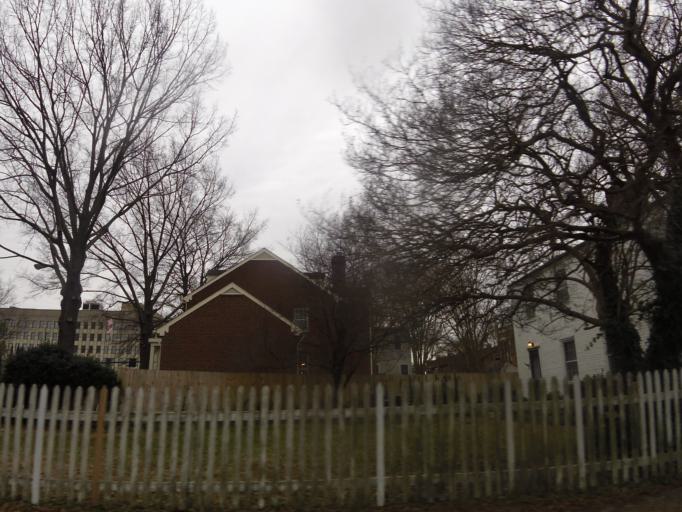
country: US
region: Virginia
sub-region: City of Portsmouth
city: Portsmouth
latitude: 36.8377
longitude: -76.2982
